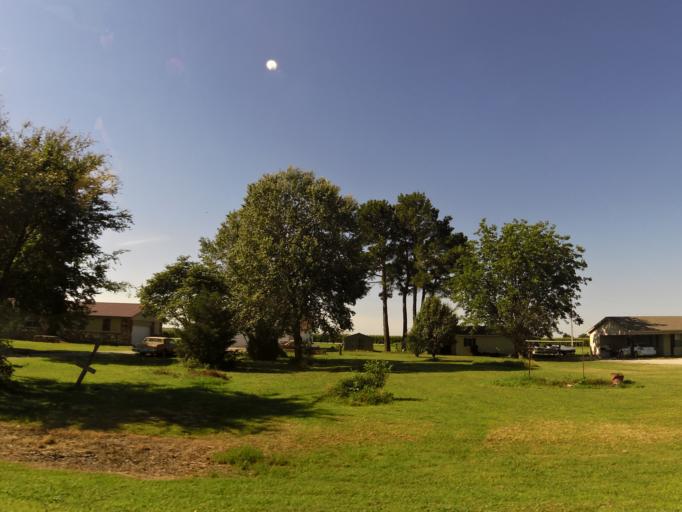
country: US
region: Arkansas
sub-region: Clay County
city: Rector
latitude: 36.4345
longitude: -90.3818
